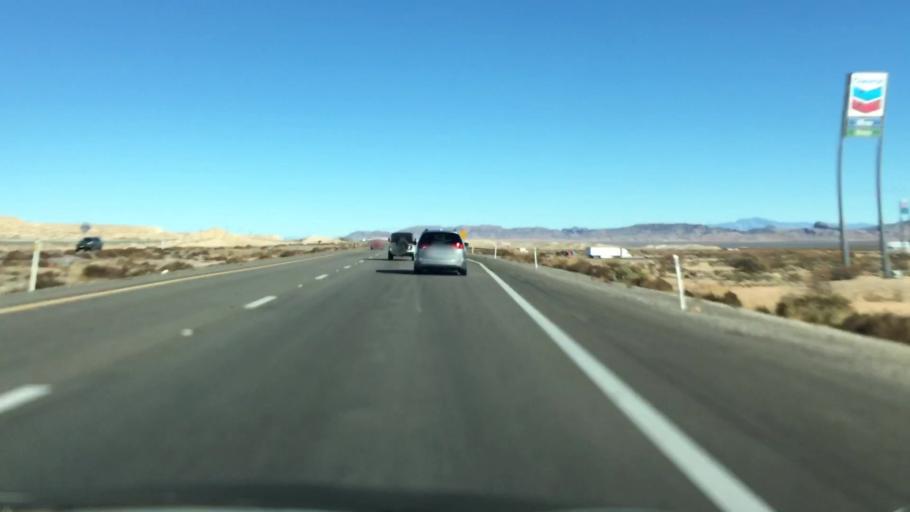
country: US
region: Nevada
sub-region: Clark County
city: Moapa Town
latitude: 36.5004
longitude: -114.7648
